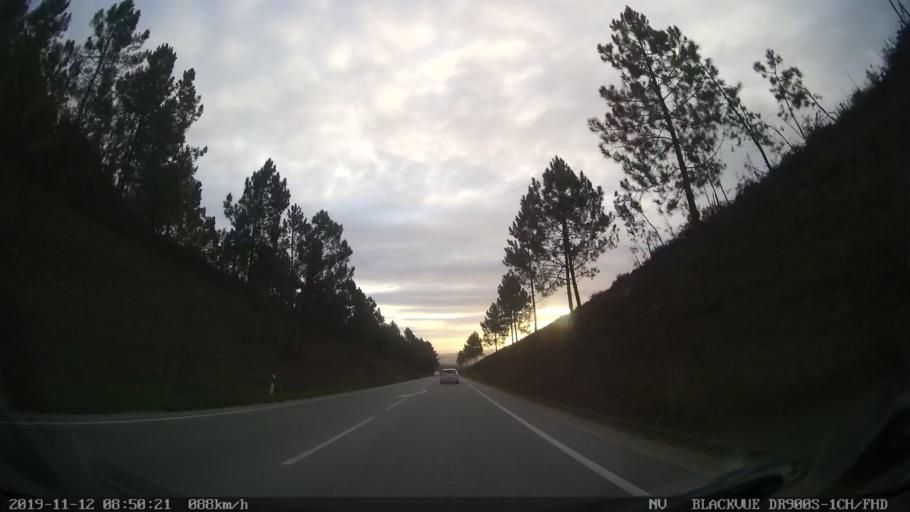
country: PT
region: Vila Real
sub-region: Sabrosa
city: Sabrosa
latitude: 41.2625
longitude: -7.6087
